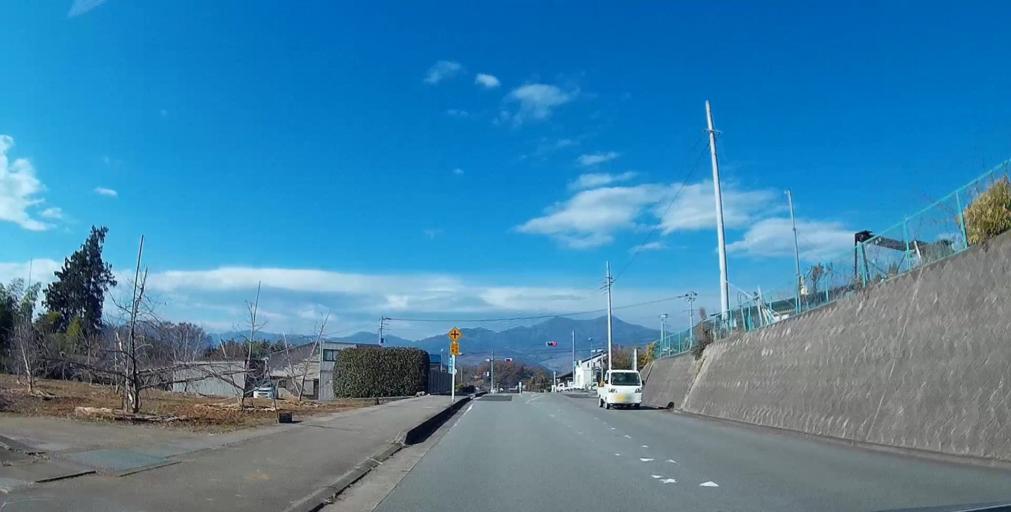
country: JP
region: Yamanashi
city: Enzan
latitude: 35.7130
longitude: 138.7453
